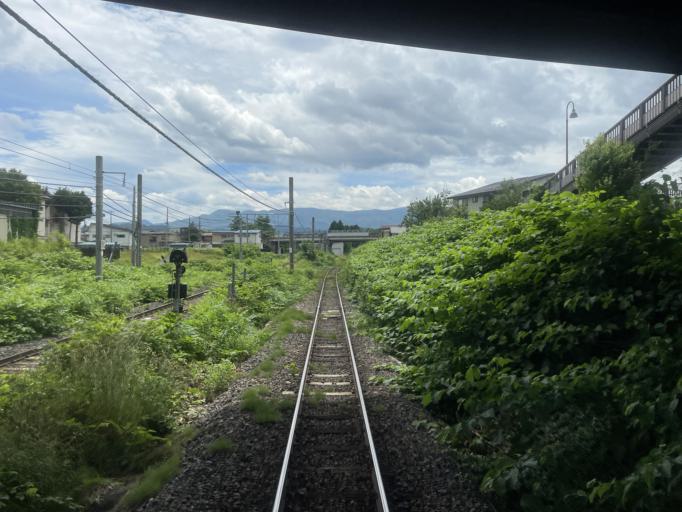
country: JP
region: Yamagata
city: Yonezawa
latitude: 37.9064
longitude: 140.1293
